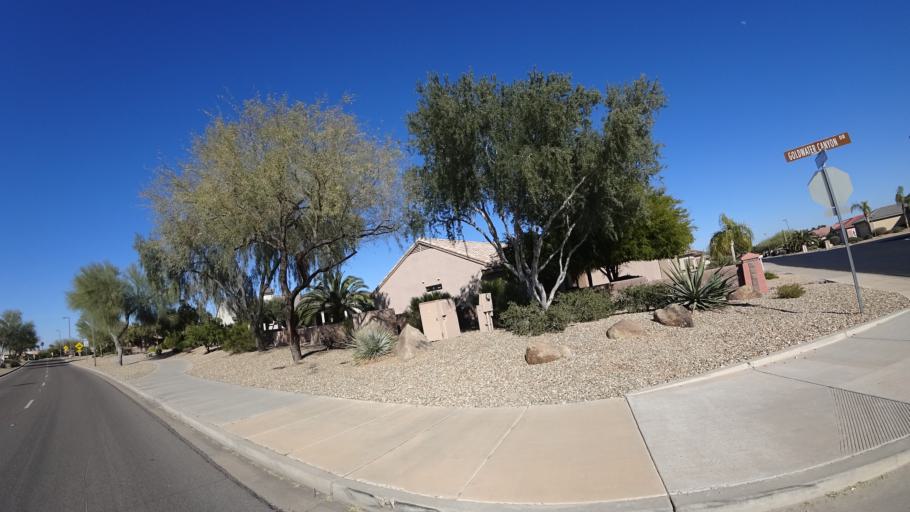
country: US
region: Arizona
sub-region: Maricopa County
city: Sun City West
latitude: 33.6508
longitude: -112.4126
